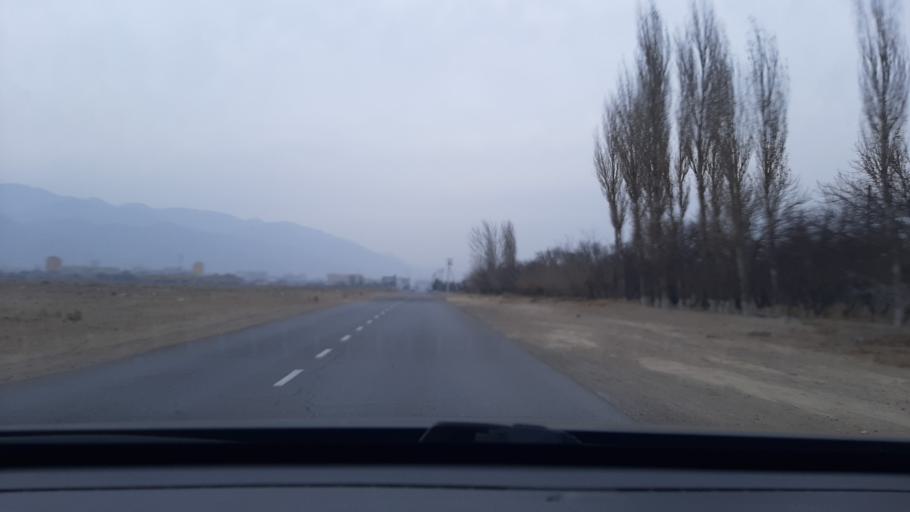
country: TJ
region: Viloyati Sughd
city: Khujand
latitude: 40.2727
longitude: 69.5764
